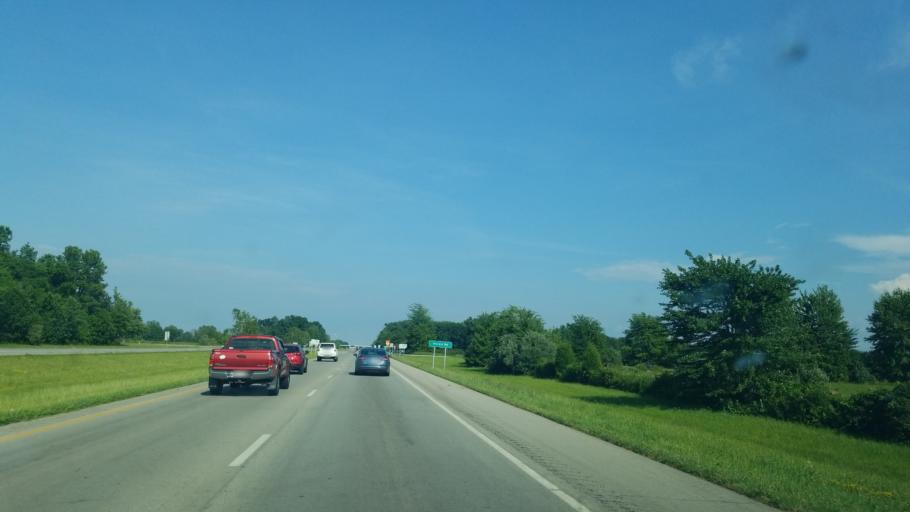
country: US
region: Ohio
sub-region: Clermont County
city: Batavia
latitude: 39.0800
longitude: -84.1378
